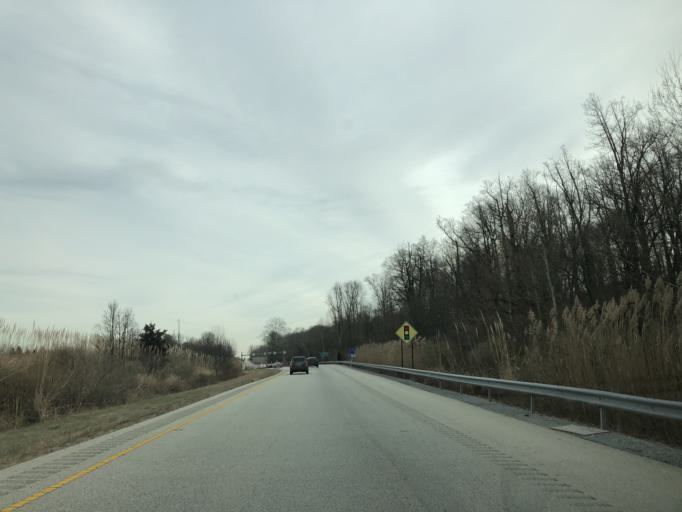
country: US
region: Pennsylvania
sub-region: Chester County
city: Exton
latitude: 40.0196
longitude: -75.6272
